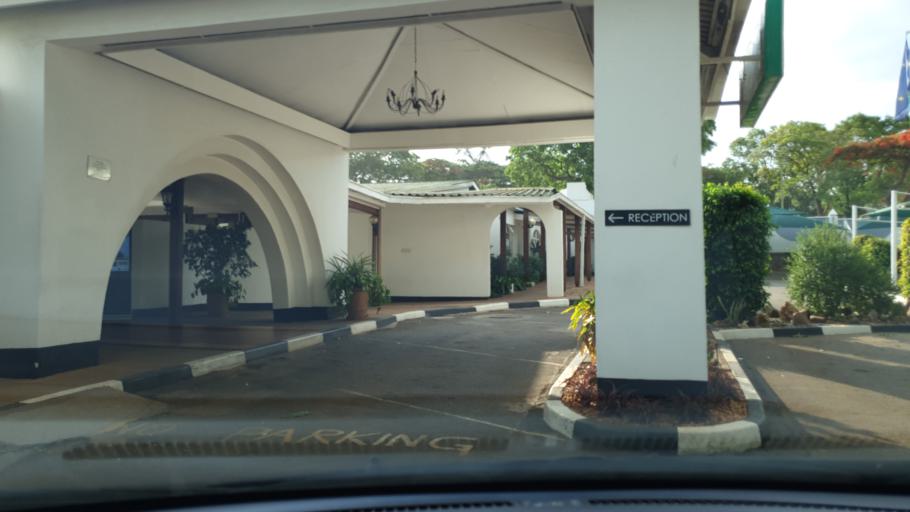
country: MW
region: Central Region
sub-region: Lilongwe District
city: Lilongwe
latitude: -13.9846
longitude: 33.7660
